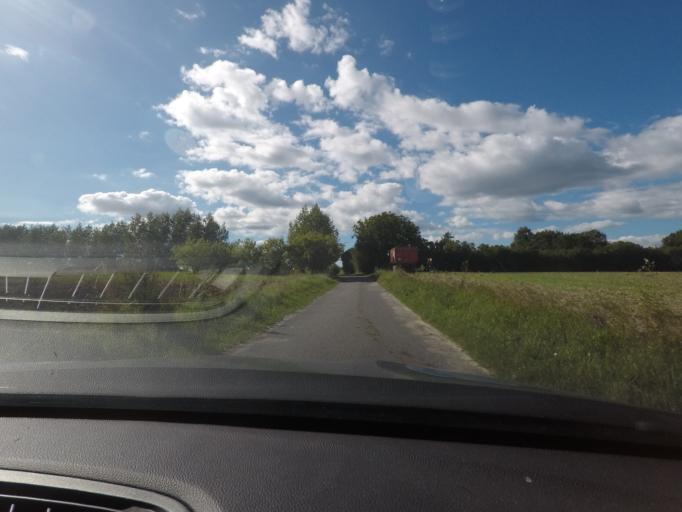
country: DK
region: Zealand
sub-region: Guldborgsund Kommune
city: Sakskobing
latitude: 54.9702
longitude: 11.5391
